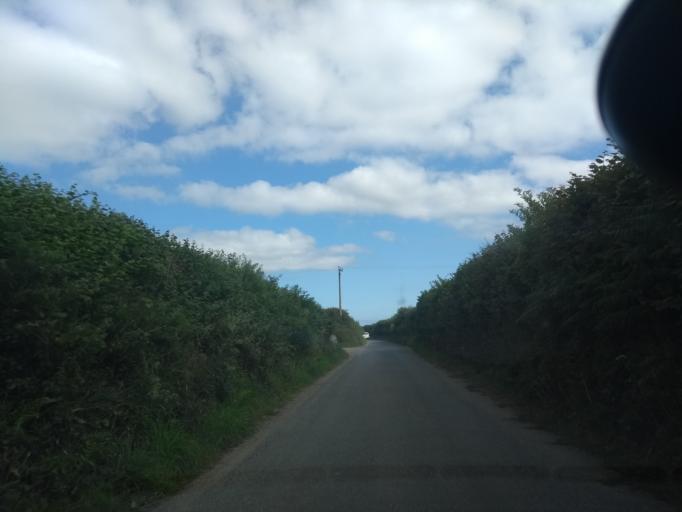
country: GB
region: England
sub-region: Devon
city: Modbury
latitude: 50.3076
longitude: -3.8728
